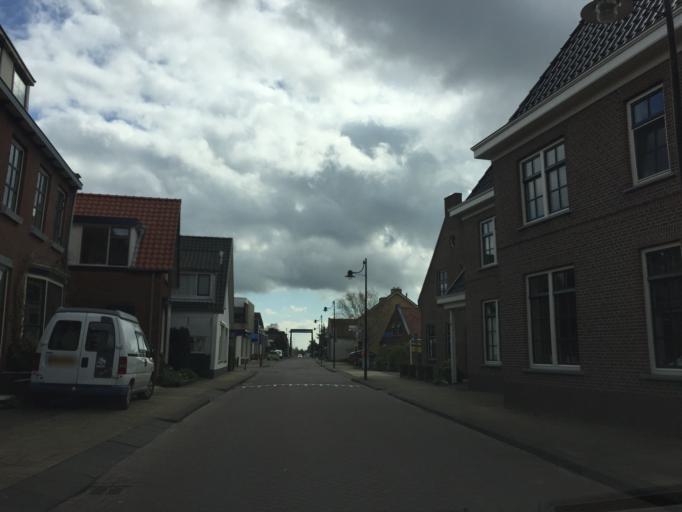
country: NL
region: South Holland
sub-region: Gemeente Rijnwoude
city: Benthuizen
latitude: 52.0962
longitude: 4.5969
